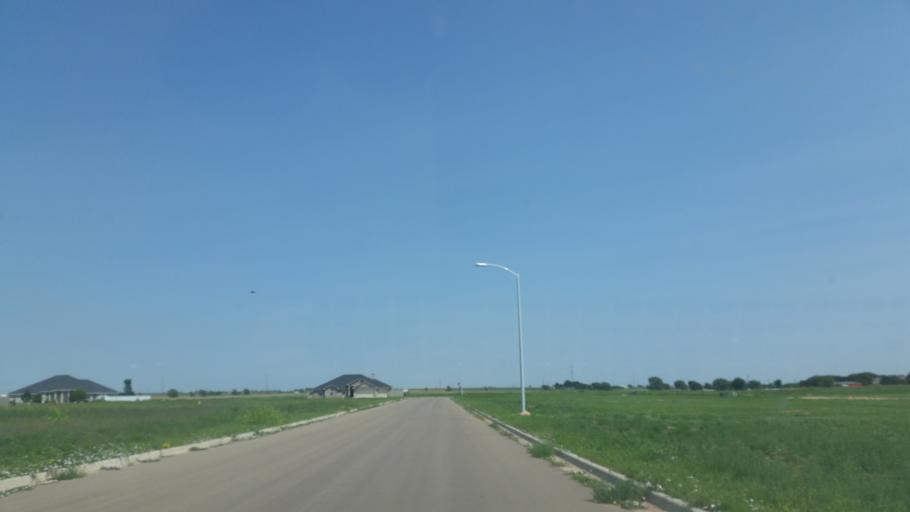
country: US
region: New Mexico
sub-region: Curry County
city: Clovis
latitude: 34.4380
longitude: -103.1724
